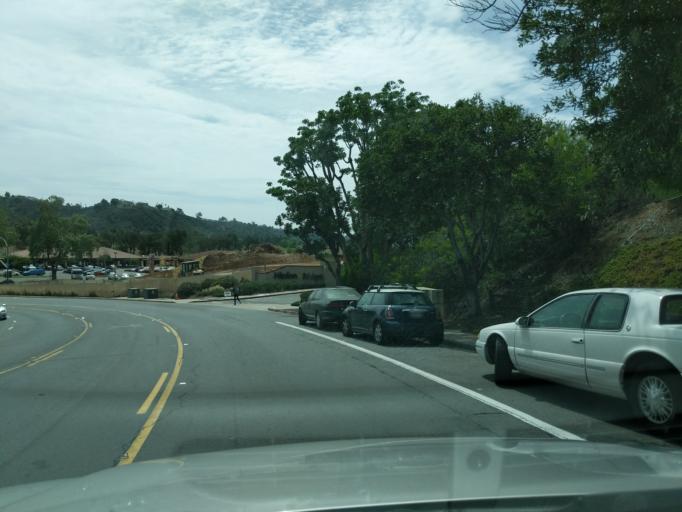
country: US
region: California
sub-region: San Diego County
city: San Diego
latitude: 32.7862
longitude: -117.1101
